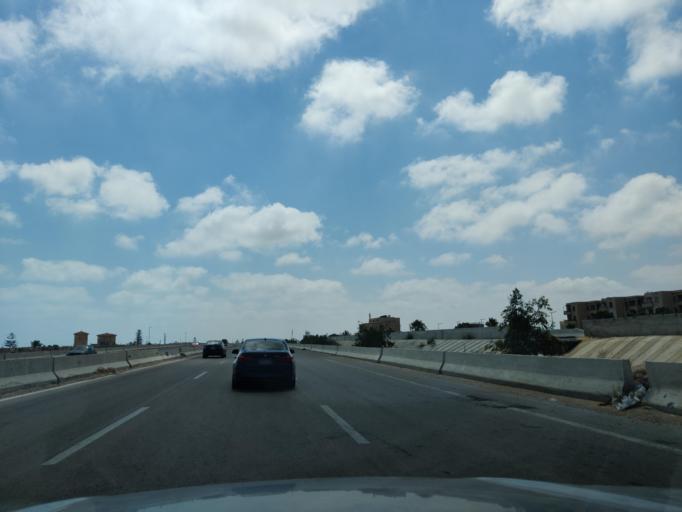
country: EG
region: Muhafazat Matruh
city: Al `Alamayn
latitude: 30.8208
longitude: 29.0142
